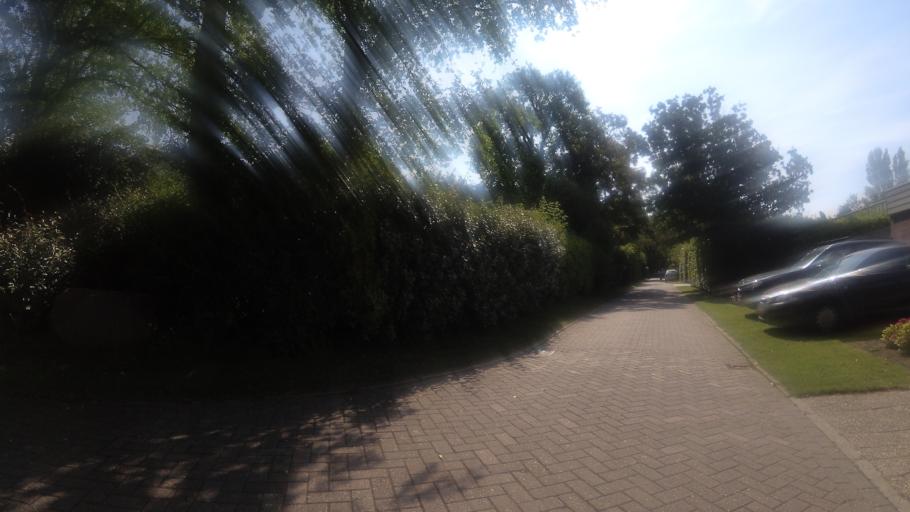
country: NL
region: Zeeland
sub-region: Gemeente Veere
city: Veere
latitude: 51.5588
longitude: 3.6829
